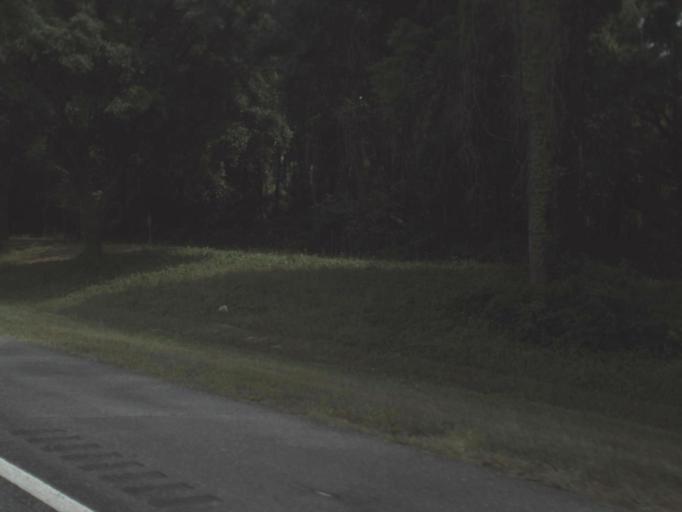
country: US
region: Florida
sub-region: Suwannee County
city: Live Oak
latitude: 30.3175
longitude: -82.9443
